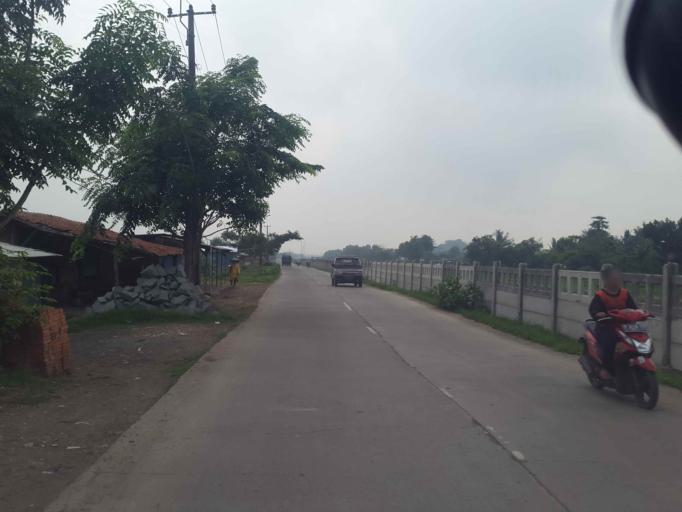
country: ID
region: West Java
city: Cikarang
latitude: -6.3461
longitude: 107.2060
